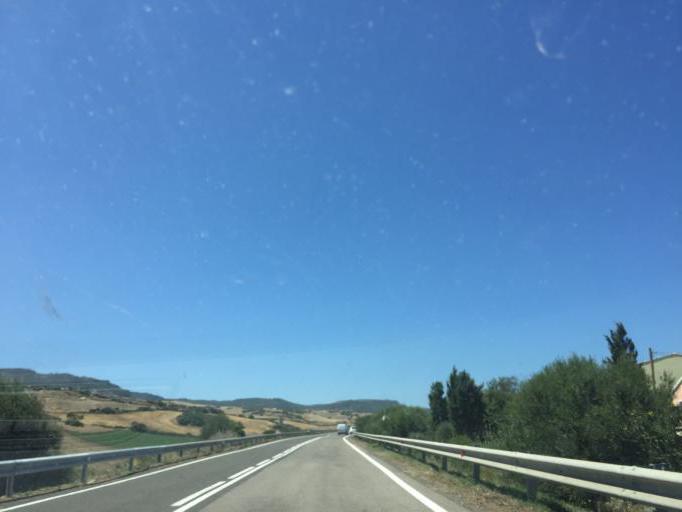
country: IT
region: Sardinia
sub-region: Provincia di Sassari
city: Valledoria
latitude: 40.9075
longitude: 8.8096
